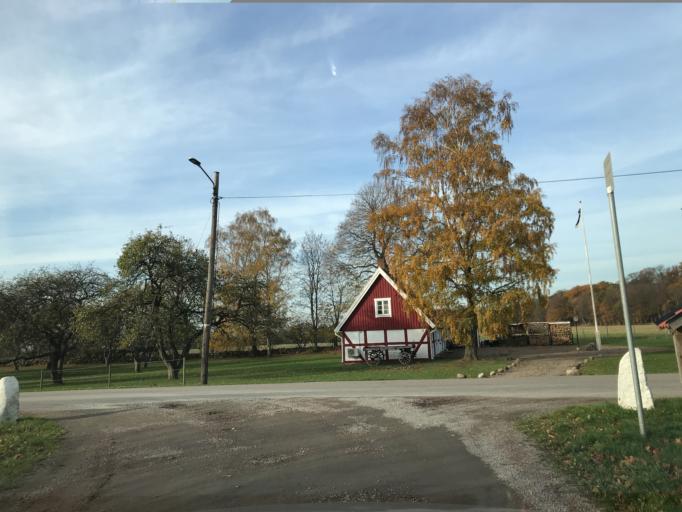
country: SE
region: Skane
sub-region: Bjuvs Kommun
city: Billesholm
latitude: 56.0704
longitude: 13.0140
